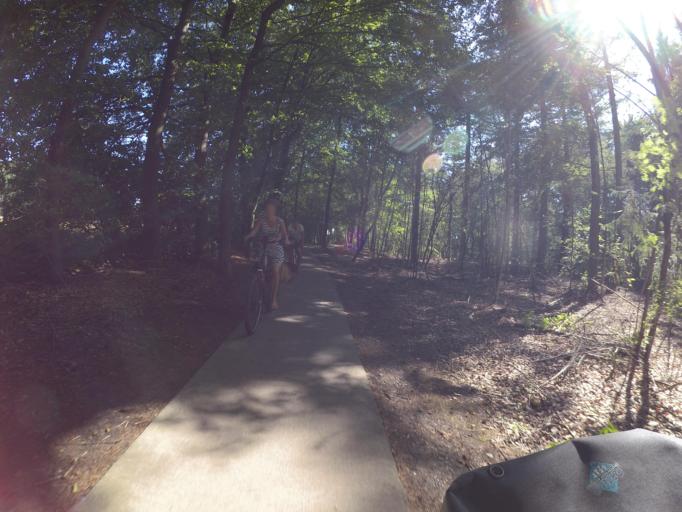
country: NL
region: Friesland
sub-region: Gemeente Gaasterlan-Sleat
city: Oudemirdum
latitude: 52.8648
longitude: 5.5569
